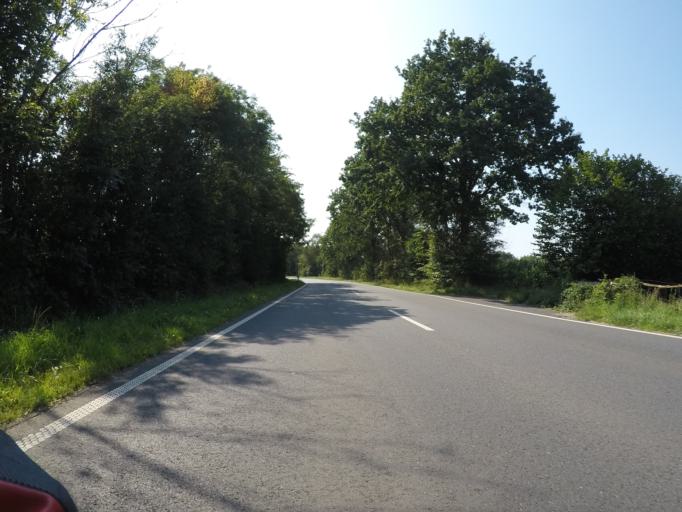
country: DE
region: Schleswig-Holstein
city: Sievershutten
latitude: 53.8423
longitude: 10.0990
